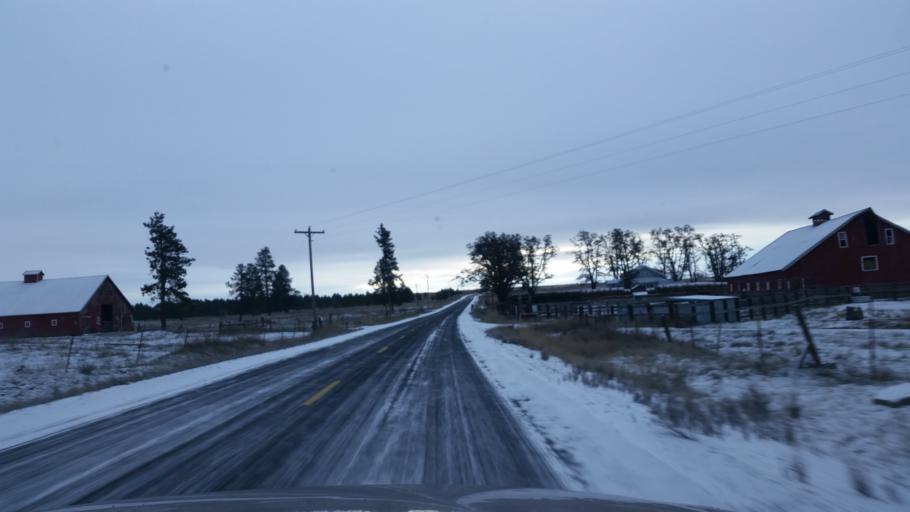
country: US
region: Washington
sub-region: Spokane County
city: Cheney
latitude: 47.4174
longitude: -117.4945
